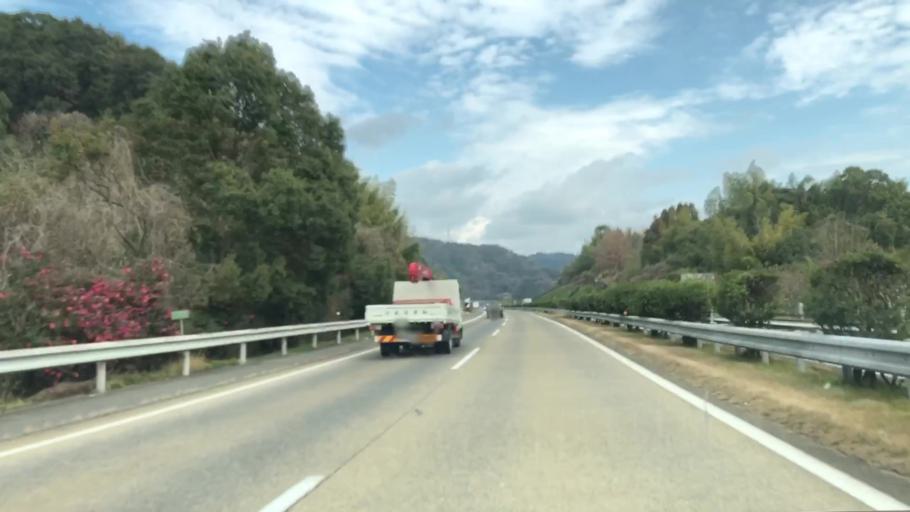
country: JP
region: Saga Prefecture
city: Kanzakimachi-kanzaki
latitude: 33.3326
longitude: 130.3221
